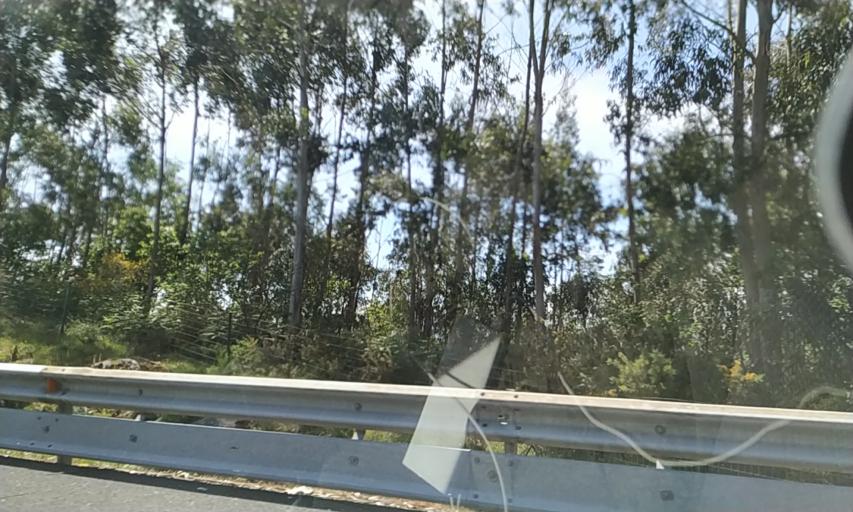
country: ES
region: Galicia
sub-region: Provincia da Coruna
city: Padron
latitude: 42.7834
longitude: -8.6445
